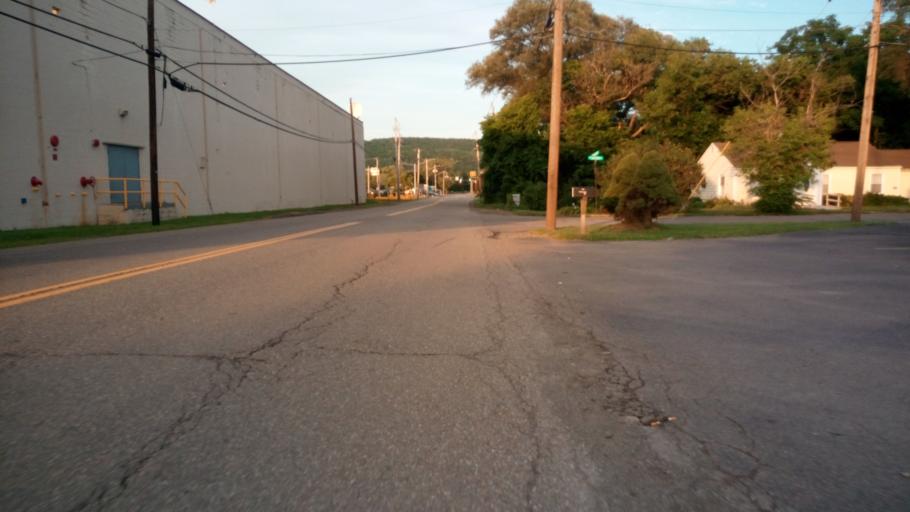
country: US
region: New York
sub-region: Chemung County
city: Horseheads
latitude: 42.1565
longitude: -76.8252
